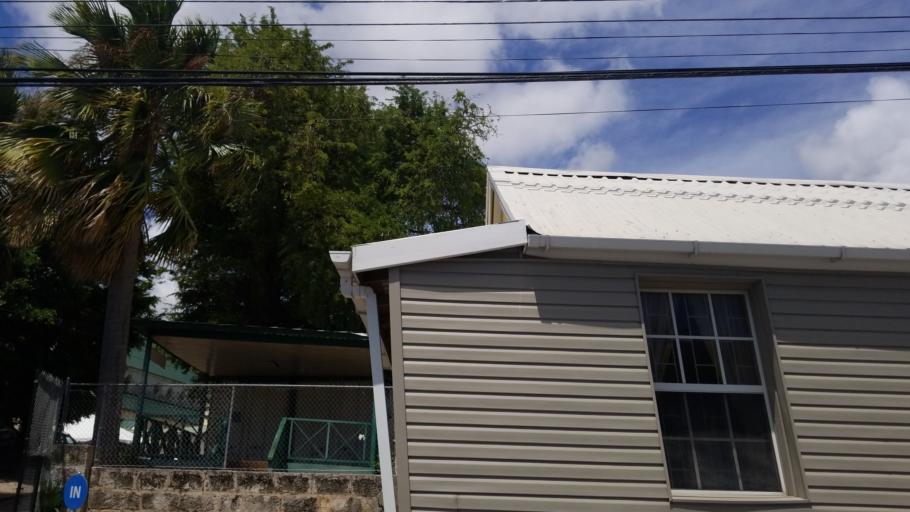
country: BB
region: Saint Michael
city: Bridgetown
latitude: 13.0911
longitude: -59.6093
